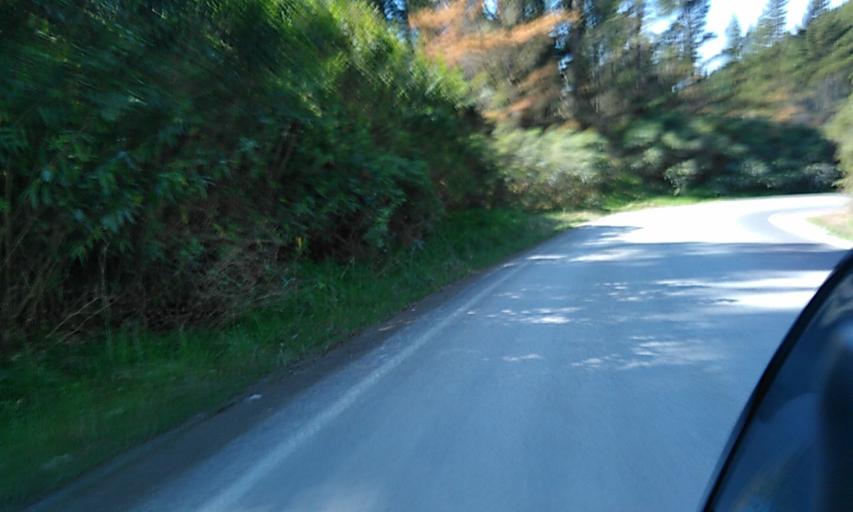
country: NZ
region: Gisborne
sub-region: Gisborne District
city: Gisborne
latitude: -38.3184
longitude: 178.1342
